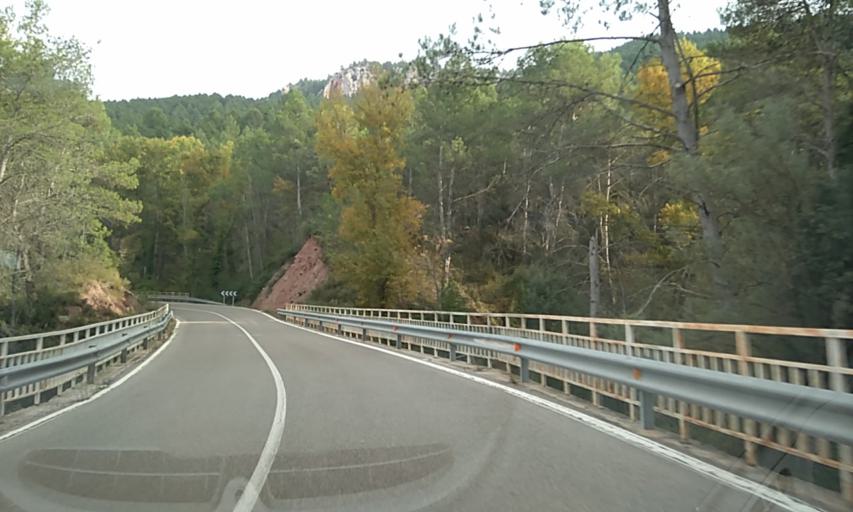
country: ES
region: Valencia
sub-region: Provincia de Castello
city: Puebla de Arenoso
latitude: 40.0866
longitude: -0.5664
